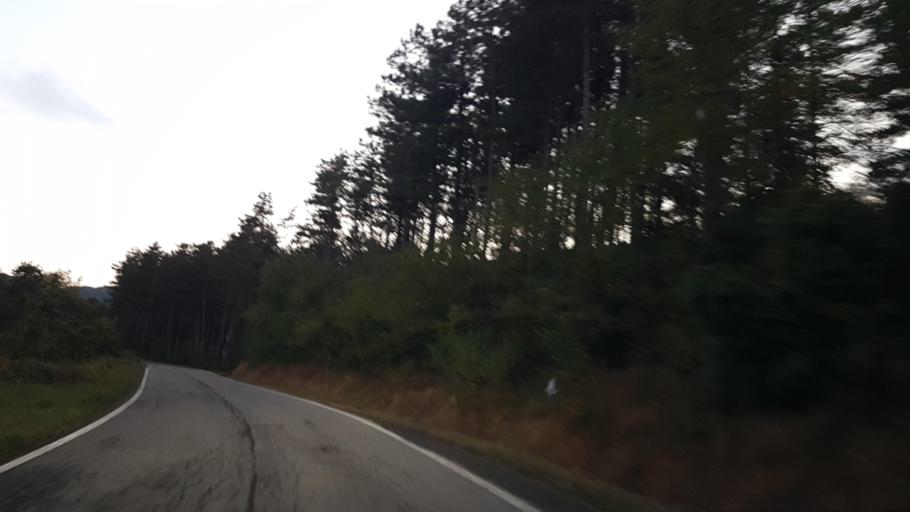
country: IT
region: Emilia-Romagna
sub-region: Provincia di Parma
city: Tornolo
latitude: 44.4359
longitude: 9.6302
